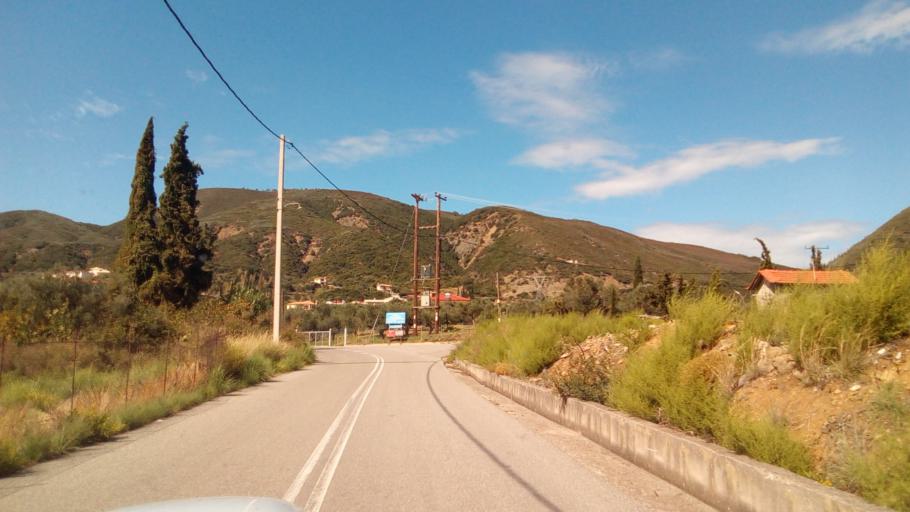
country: GR
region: West Greece
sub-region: Nomos Aitolias kai Akarnanias
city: Antirrio
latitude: 38.3690
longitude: 21.7758
